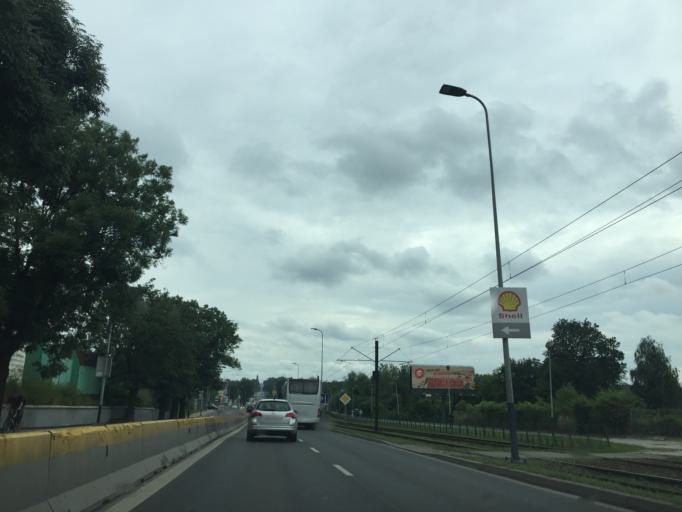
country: PL
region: Lesser Poland Voivodeship
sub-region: Krakow
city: Krakow
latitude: 50.0243
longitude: 19.9339
